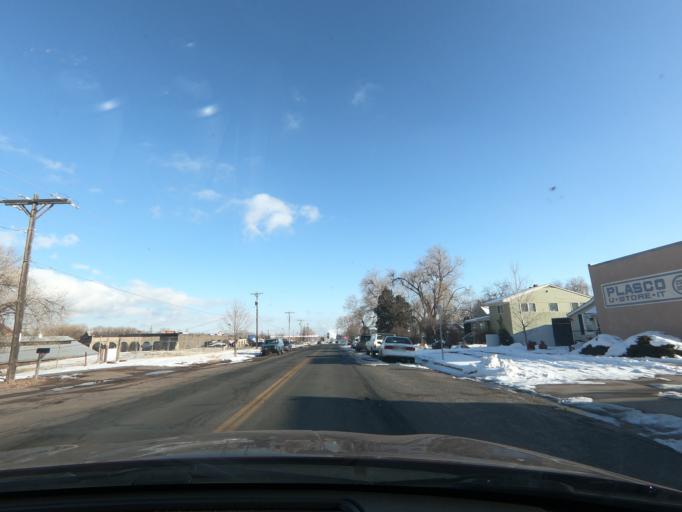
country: US
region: Colorado
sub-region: El Paso County
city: Colorado Springs
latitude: 38.8402
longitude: -104.8617
